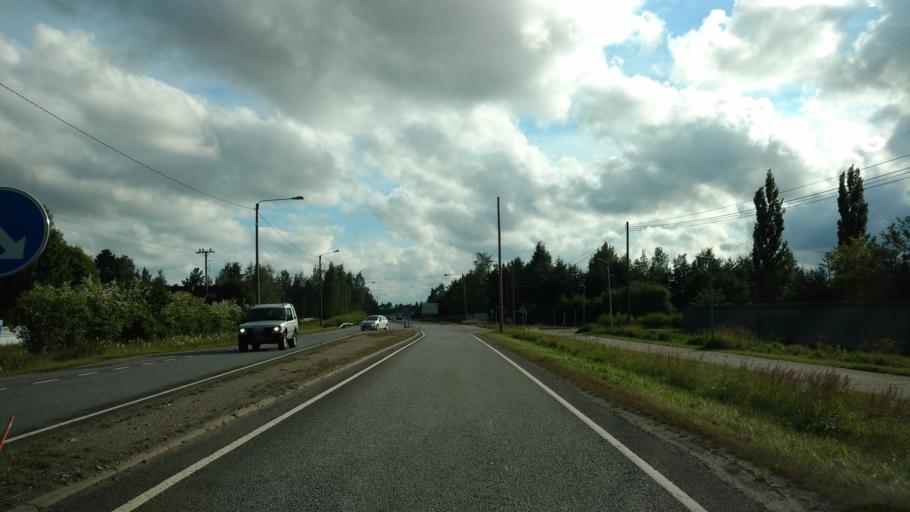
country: FI
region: Varsinais-Suomi
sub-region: Salo
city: Salo
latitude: 60.3985
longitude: 23.1398
